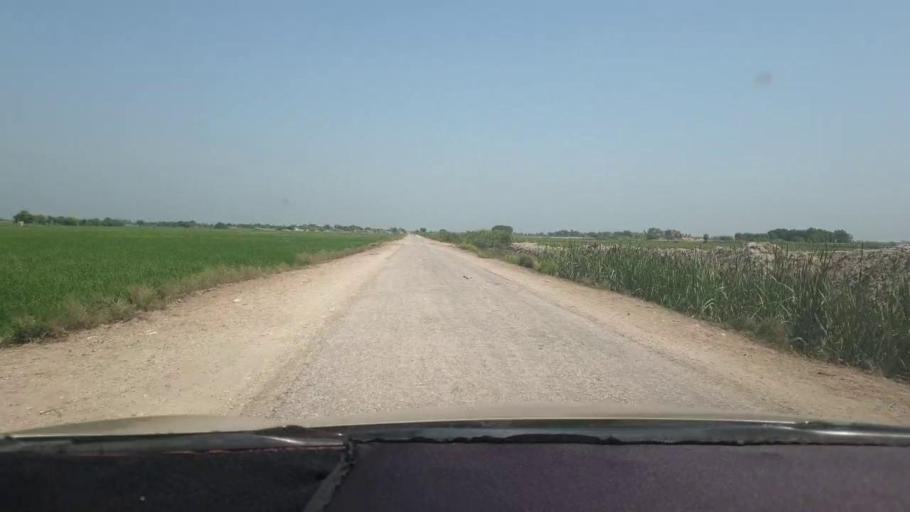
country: PK
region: Sindh
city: Miro Khan
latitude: 27.6885
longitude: 68.0829
